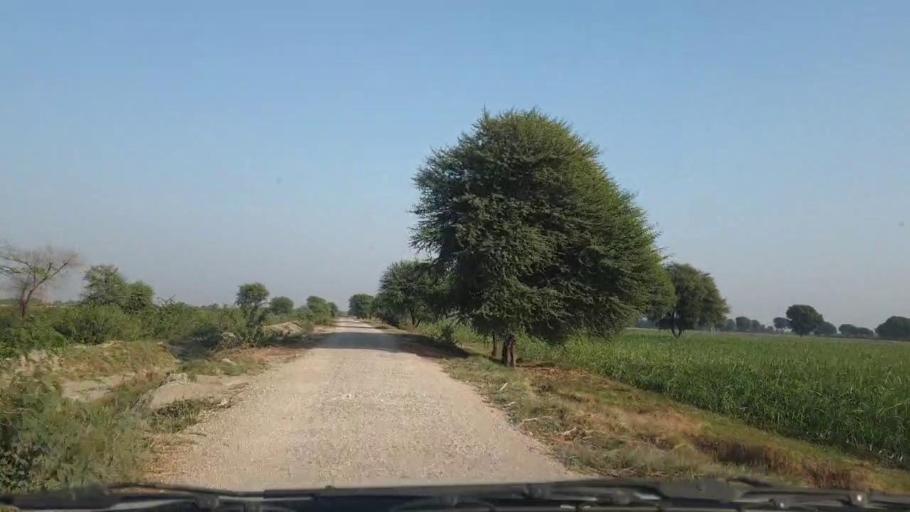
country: PK
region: Sindh
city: Chambar
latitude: 25.2160
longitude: 68.6787
